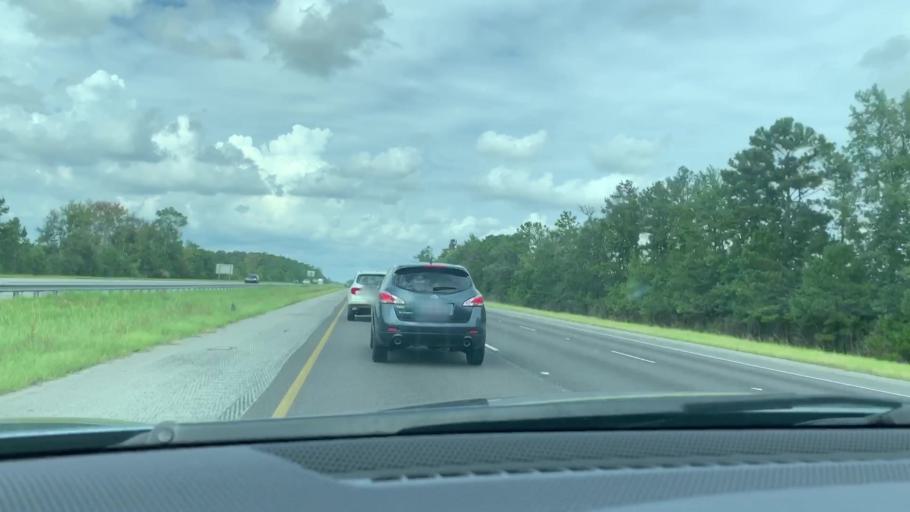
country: US
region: Georgia
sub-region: Liberty County
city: Midway
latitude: 31.6655
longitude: -81.3924
